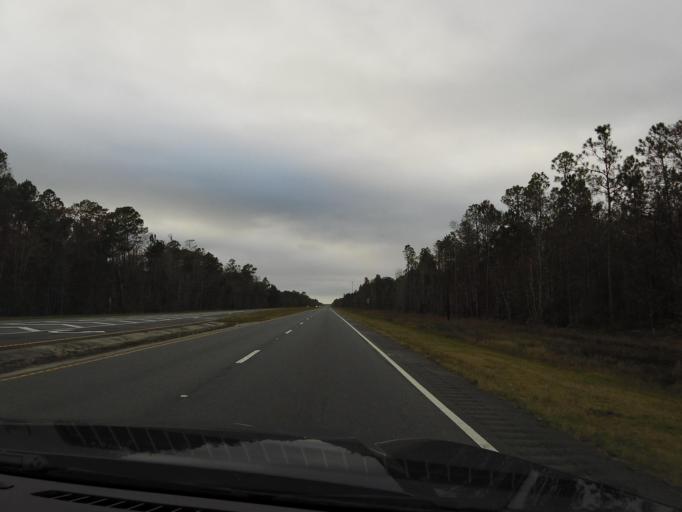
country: US
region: Georgia
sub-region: Charlton County
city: Folkston
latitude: 30.8951
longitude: -82.0540
